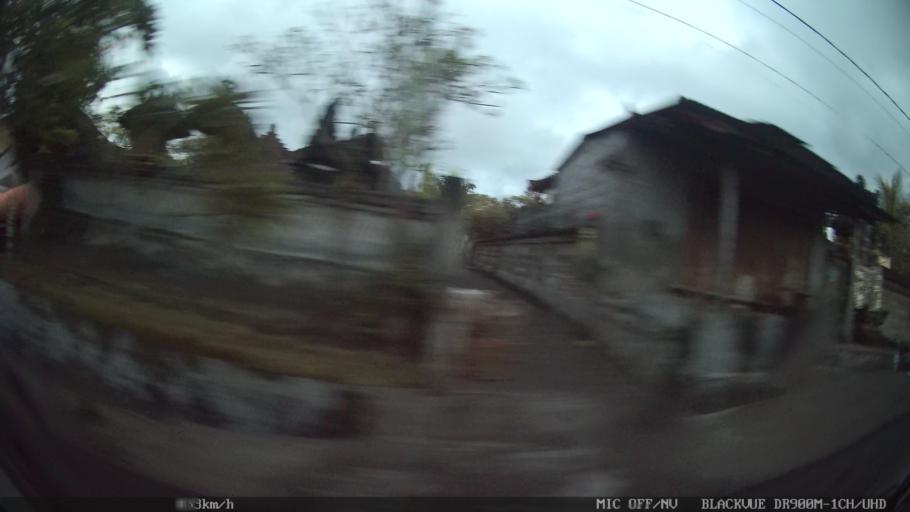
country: ID
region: Bali
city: Banjar Pasekan
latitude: -8.6201
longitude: 115.2728
